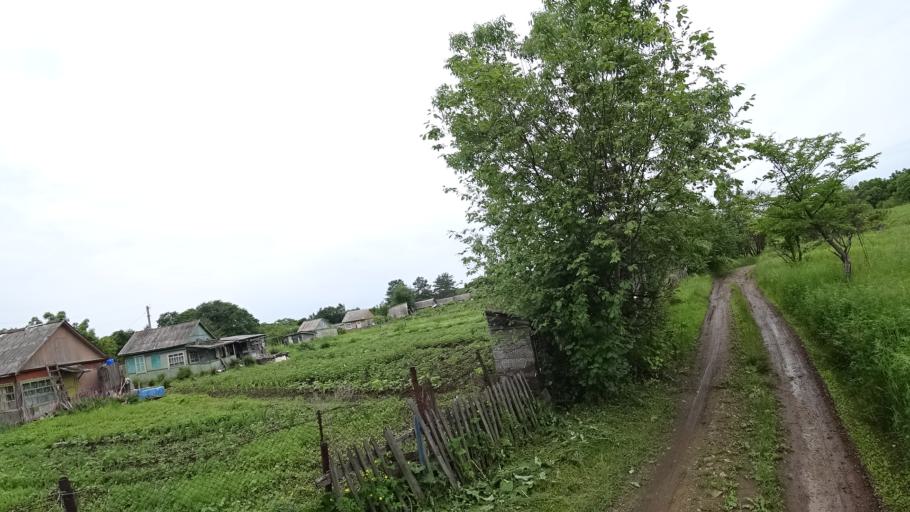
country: RU
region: Primorskiy
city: Novosysoyevka
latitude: 44.2105
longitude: 133.3272
